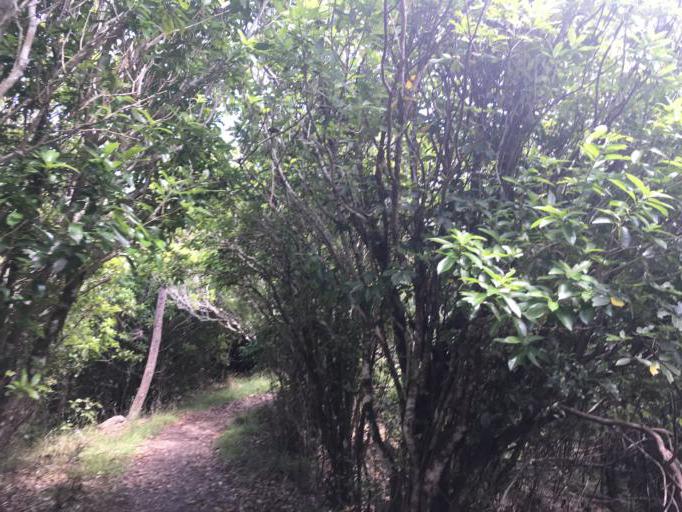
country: NZ
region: Marlborough
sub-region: Marlborough District
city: Picton
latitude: -41.2137
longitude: 173.9912
